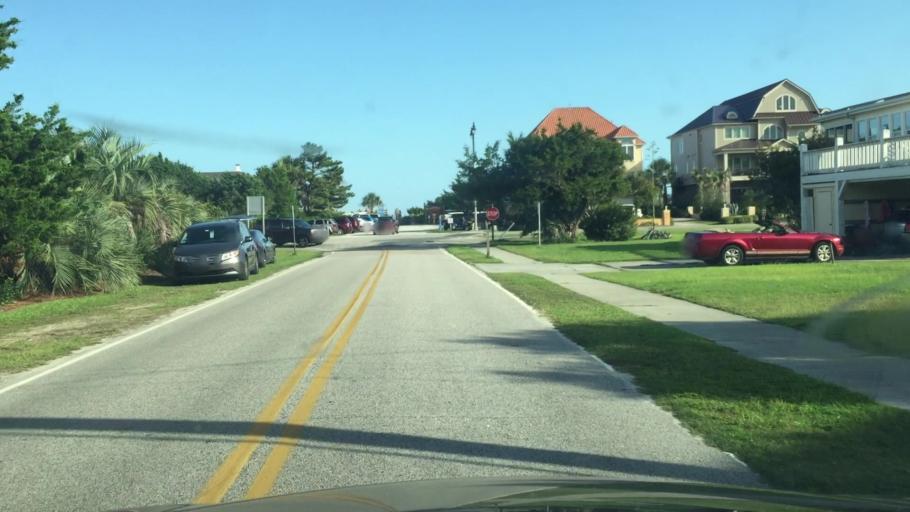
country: US
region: South Carolina
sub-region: Horry County
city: North Myrtle Beach
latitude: 33.8227
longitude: -78.6633
